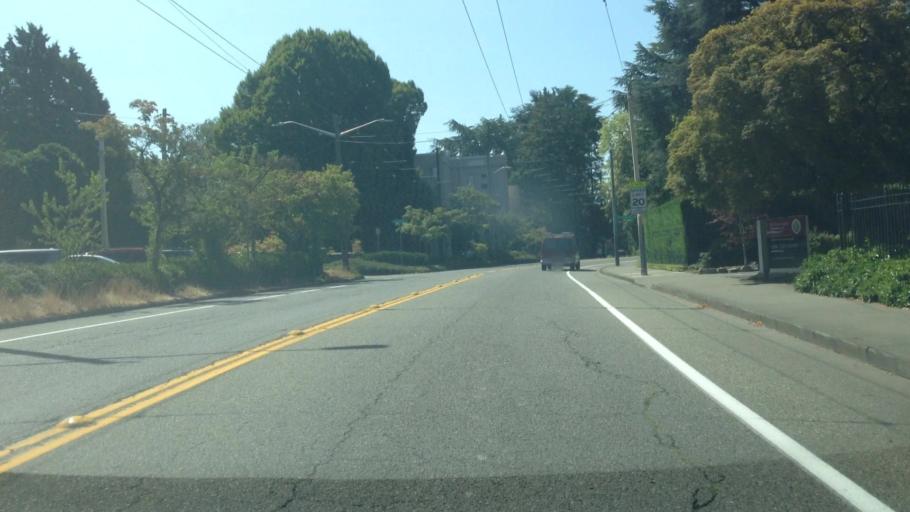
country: US
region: Washington
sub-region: King County
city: Seattle
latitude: 47.6336
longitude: -122.3200
